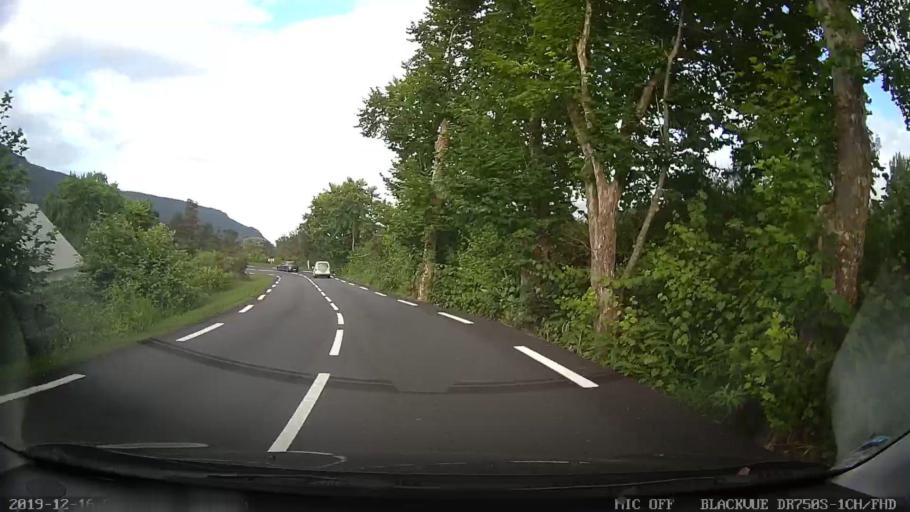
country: RE
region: Reunion
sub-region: Reunion
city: Cilaos
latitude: -21.1504
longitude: 55.6152
